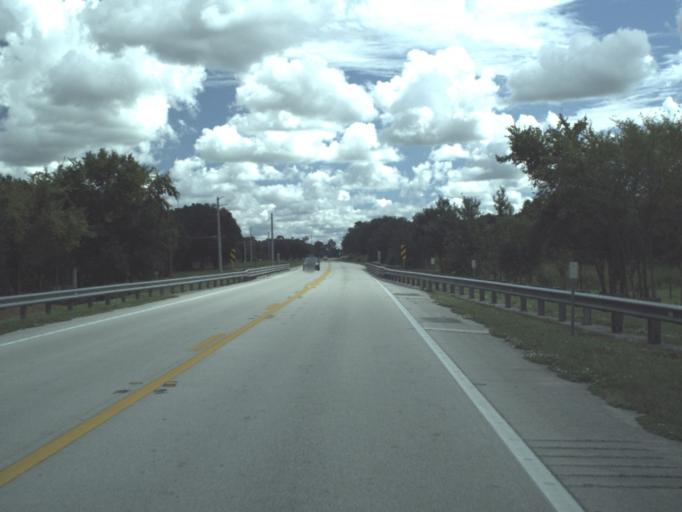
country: US
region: Florida
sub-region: DeSoto County
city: Southeast Arcadia
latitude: 27.2088
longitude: -81.8053
